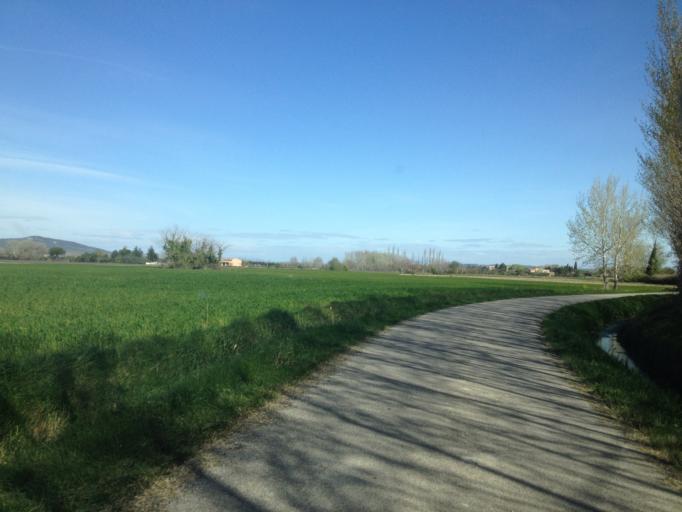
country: FR
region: Provence-Alpes-Cote d'Azur
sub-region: Departement du Vaucluse
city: Caderousse
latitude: 44.1198
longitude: 4.7584
